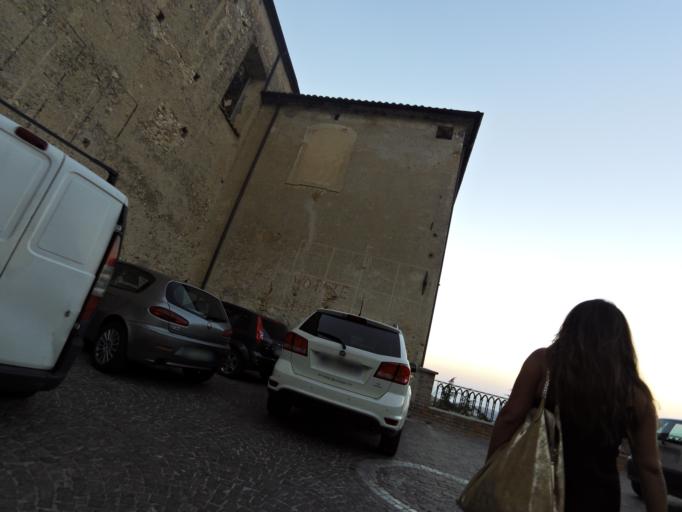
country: IT
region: Calabria
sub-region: Provincia di Reggio Calabria
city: Stilo
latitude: 38.4798
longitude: 16.4694
